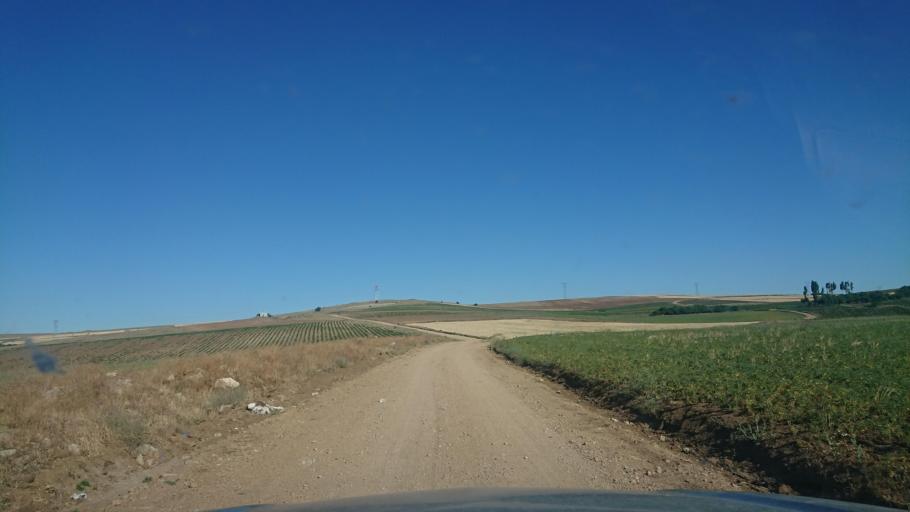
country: TR
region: Aksaray
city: Agacoren
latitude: 38.8277
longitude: 33.9542
